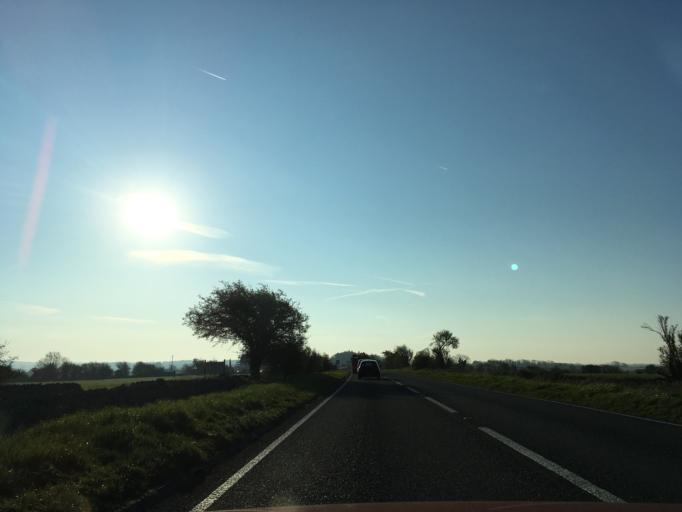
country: GB
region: England
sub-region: Gloucestershire
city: Bourton on the Water
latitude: 51.8122
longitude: -1.7313
